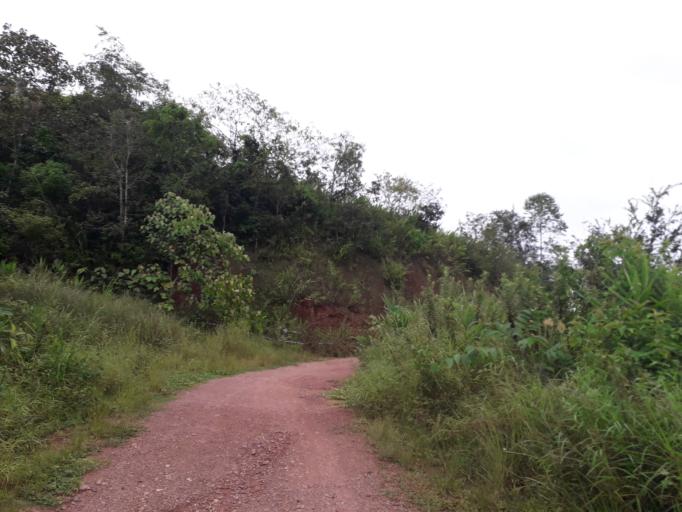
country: CN
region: Yunnan
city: Menglie
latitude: 22.2580
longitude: 101.5968
